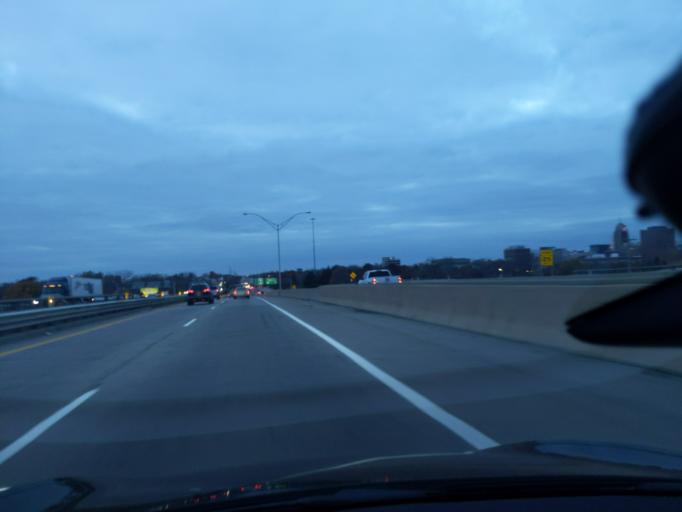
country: US
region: Michigan
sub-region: Ingham County
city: Lansing
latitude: 42.7257
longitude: -84.5411
